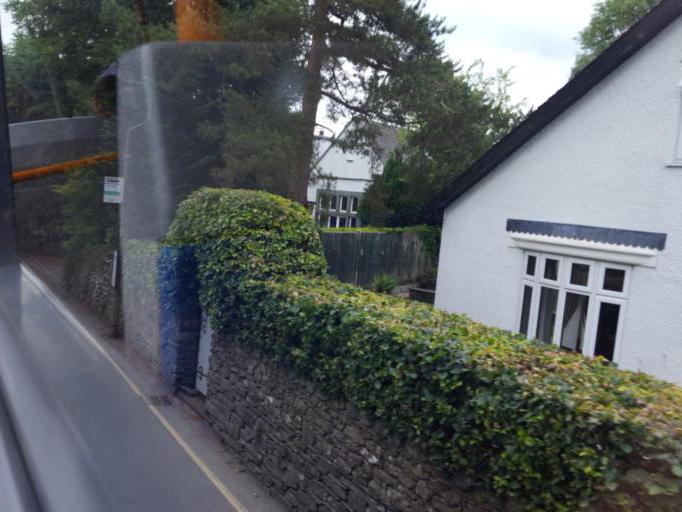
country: GB
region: England
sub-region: Cumbria
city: Ambleside
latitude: 54.4569
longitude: -3.0215
